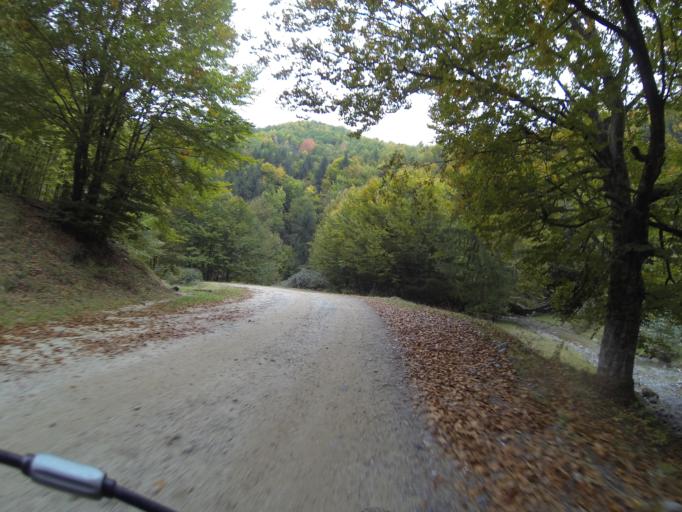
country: RO
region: Gorj
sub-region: Comuna Tismana
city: Sohodol
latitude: 45.0729
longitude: 22.8878
